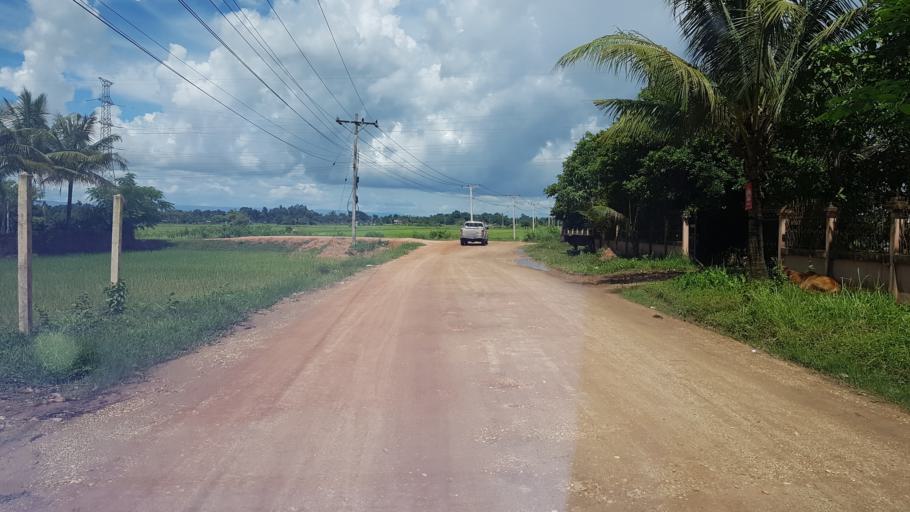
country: LA
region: Vientiane
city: Vientiane
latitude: 18.2153
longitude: 102.5007
